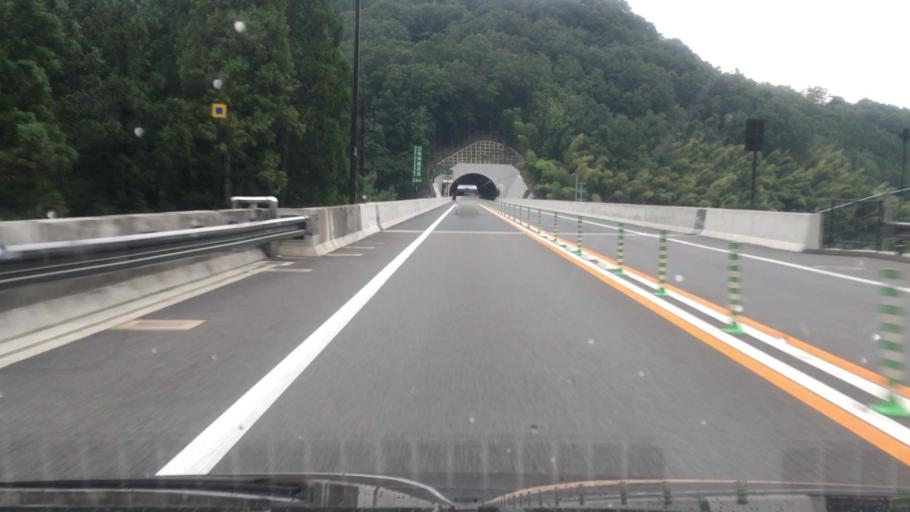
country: JP
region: Hyogo
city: Toyooka
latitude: 35.4485
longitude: 134.7659
